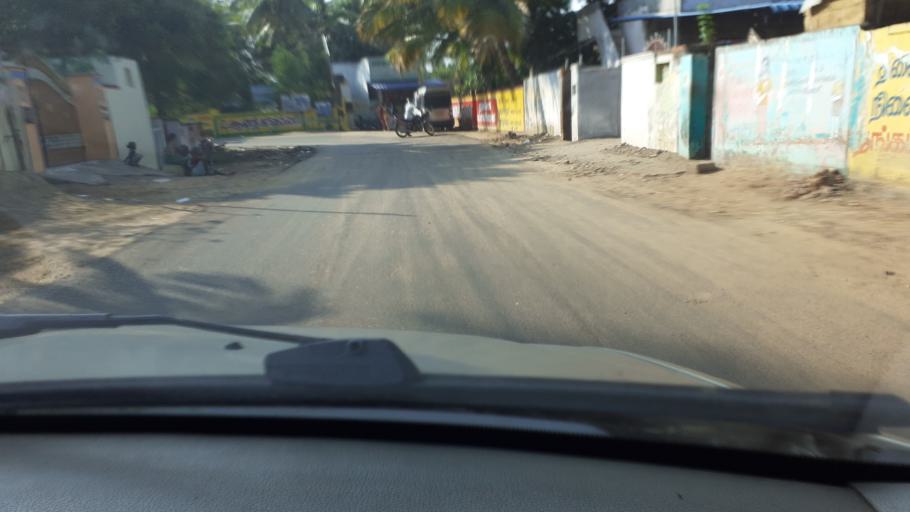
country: IN
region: Tamil Nadu
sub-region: Thoothukkudi
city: Eral
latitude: 8.5788
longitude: 78.0299
